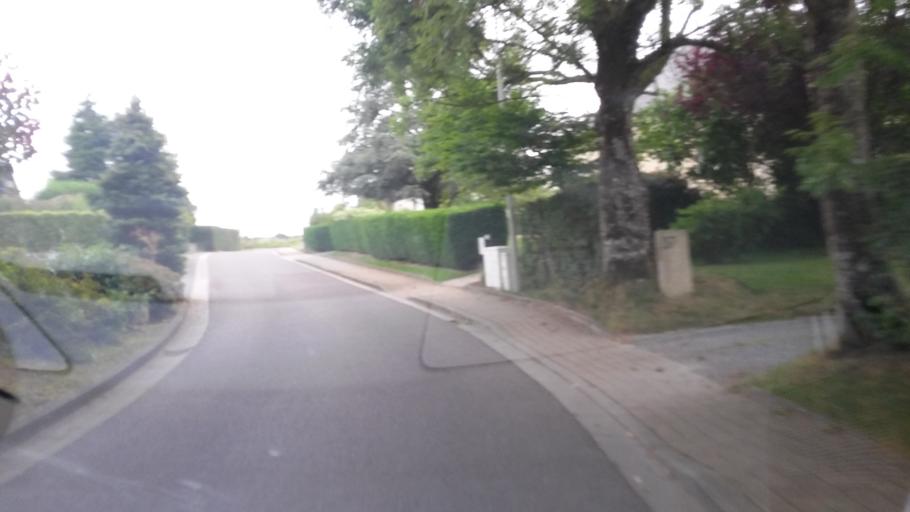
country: BE
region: Wallonia
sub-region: Province du Luxembourg
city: Arlon
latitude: 49.6849
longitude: 5.8415
